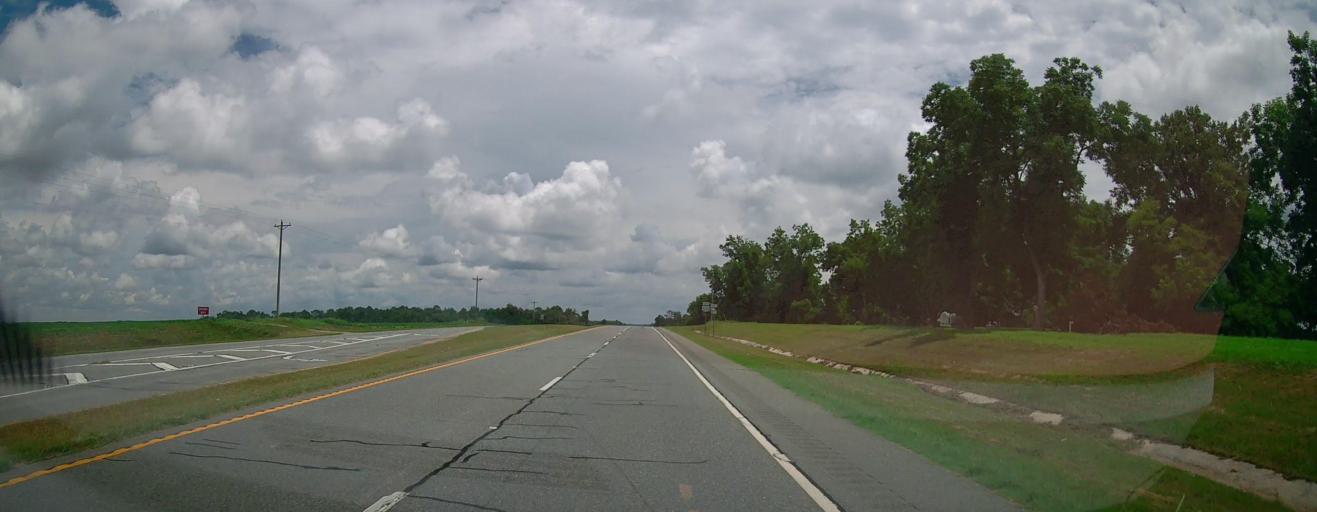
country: US
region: Georgia
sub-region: Pulaski County
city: Hawkinsville
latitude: 32.2324
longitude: -83.3676
